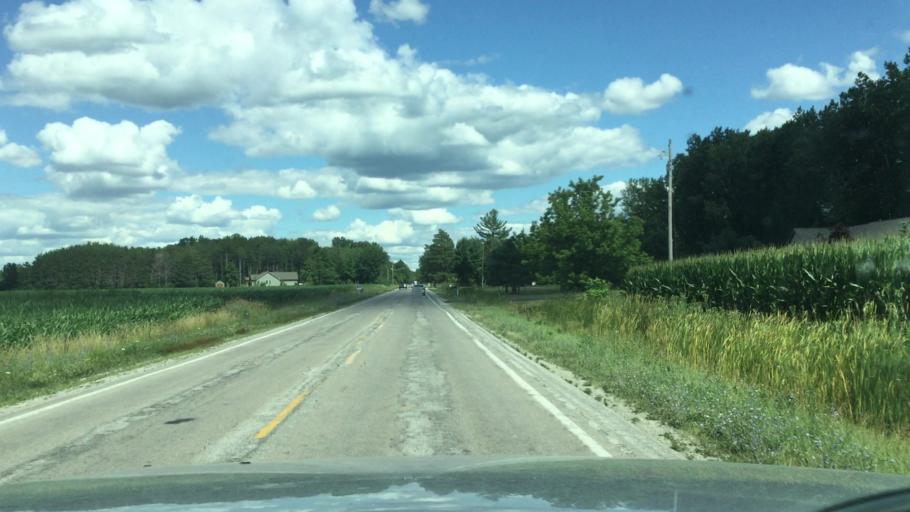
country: US
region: Michigan
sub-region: Saginaw County
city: Hemlock
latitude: 43.3798
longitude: -84.1566
